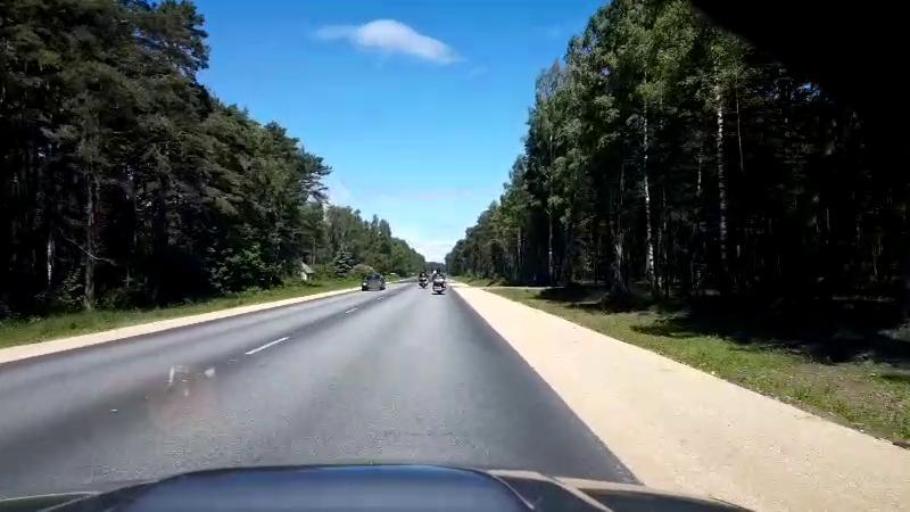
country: LV
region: Salacgrivas
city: Salacgriva
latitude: 57.8037
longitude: 24.3492
